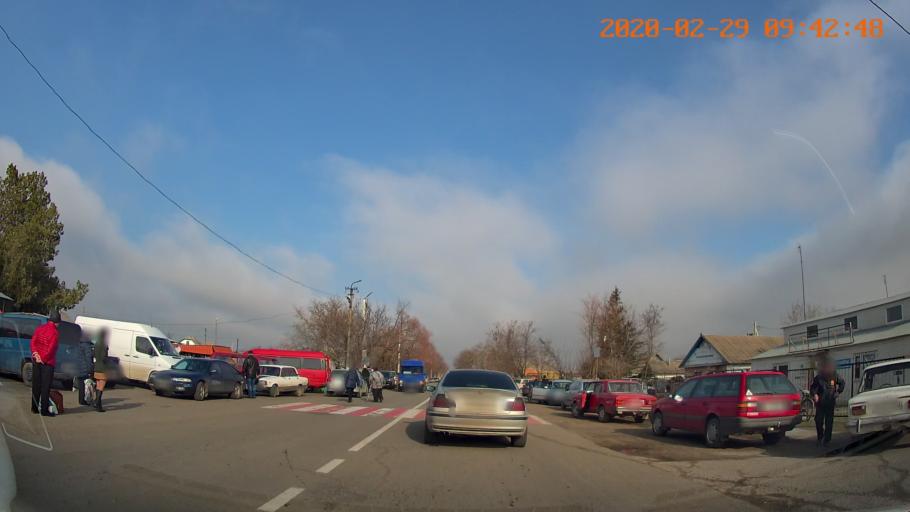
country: MD
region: Telenesti
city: Crasnoe
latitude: 46.6421
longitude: 29.8232
